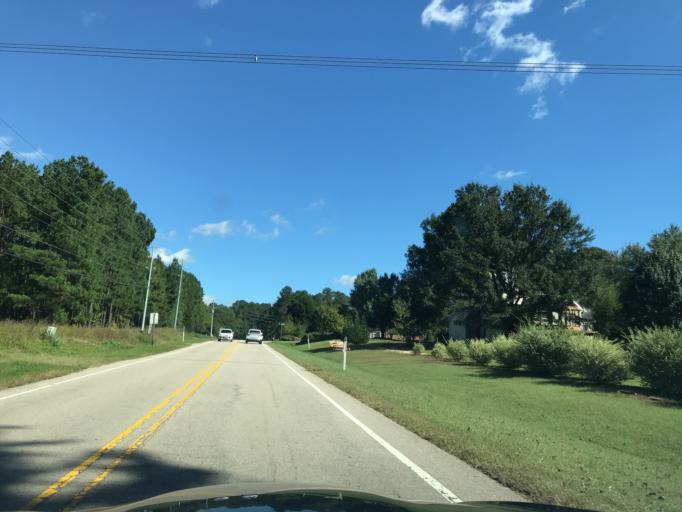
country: US
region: North Carolina
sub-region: Wake County
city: Wake Forest
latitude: 35.9221
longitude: -78.5179
